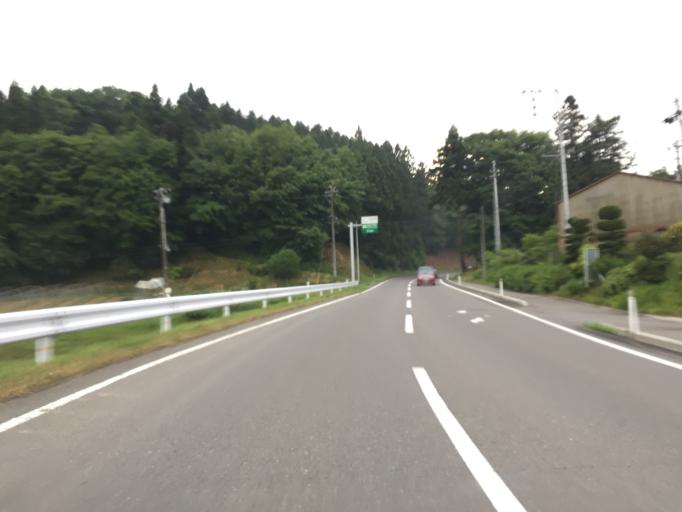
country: JP
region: Fukushima
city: Ishikawa
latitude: 37.2097
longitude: 140.4485
